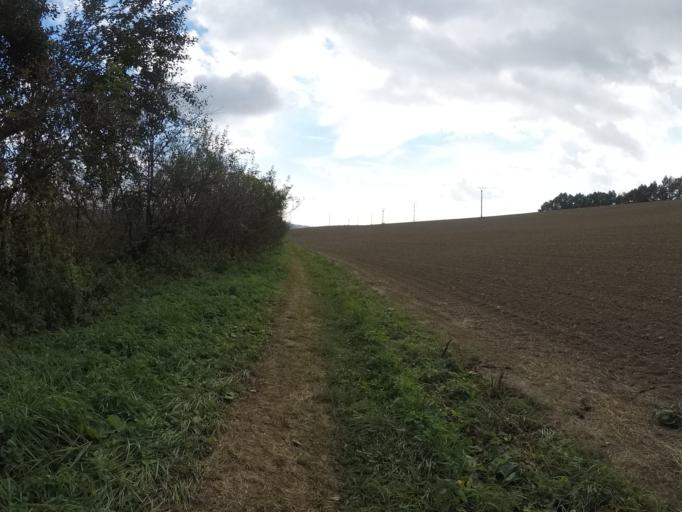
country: SK
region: Presovsky
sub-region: Okres Presov
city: Presov
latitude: 48.9325
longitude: 21.1796
